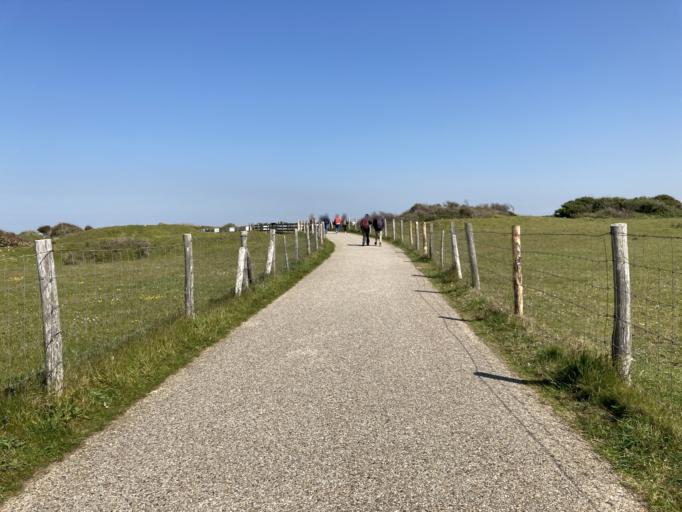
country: FR
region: Nord-Pas-de-Calais
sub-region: Departement du Pas-de-Calais
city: Ambleteuse
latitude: 50.8699
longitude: 1.5844
